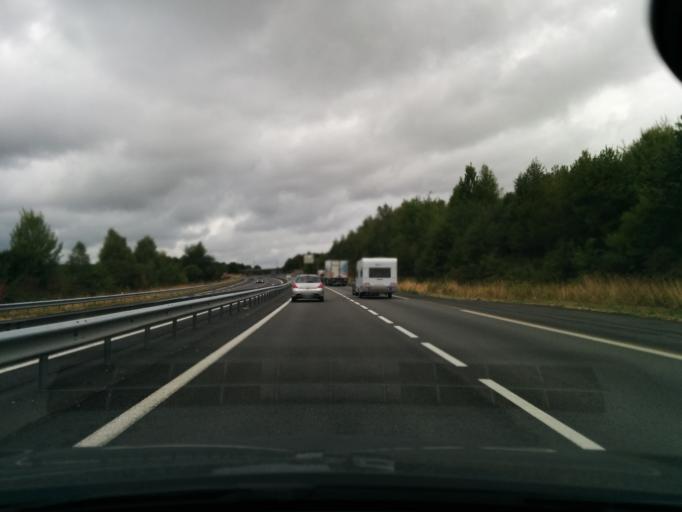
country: FR
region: Limousin
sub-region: Departement de la Haute-Vienne
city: Saint-Germain-les-Belles
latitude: 45.5222
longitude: 1.5162
